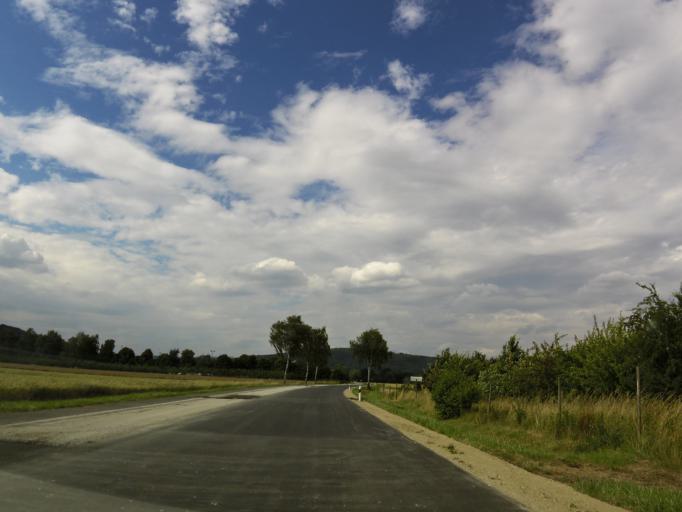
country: DE
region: North Rhine-Westphalia
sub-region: Regierungsbezirk Detmold
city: Hoexter
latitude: 51.7638
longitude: 9.3872
